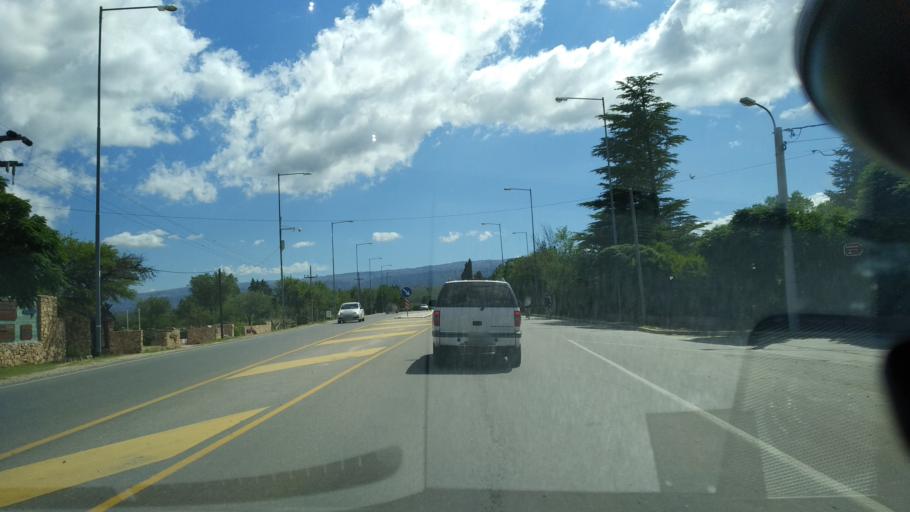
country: AR
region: Cordoba
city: Mina Clavero
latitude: -31.7938
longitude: -65.0024
